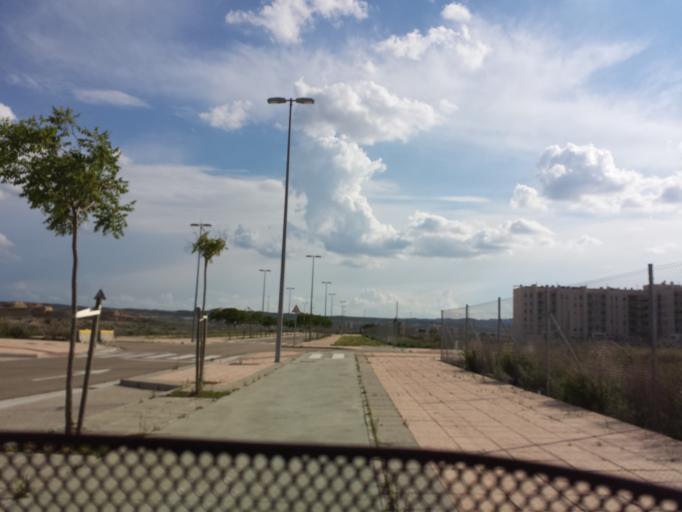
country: ES
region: Aragon
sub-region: Provincia de Zaragoza
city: Montecanal
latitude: 41.6379
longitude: -0.9516
